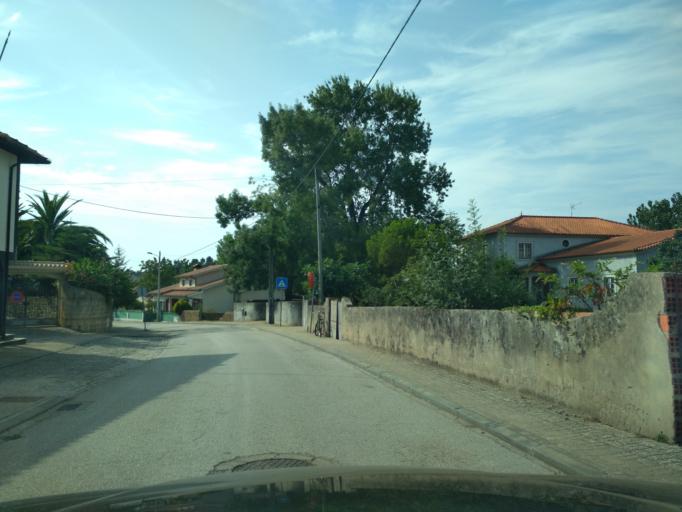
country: PT
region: Aveiro
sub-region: Mealhada
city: Mealhada
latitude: 40.3621
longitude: -8.5053
